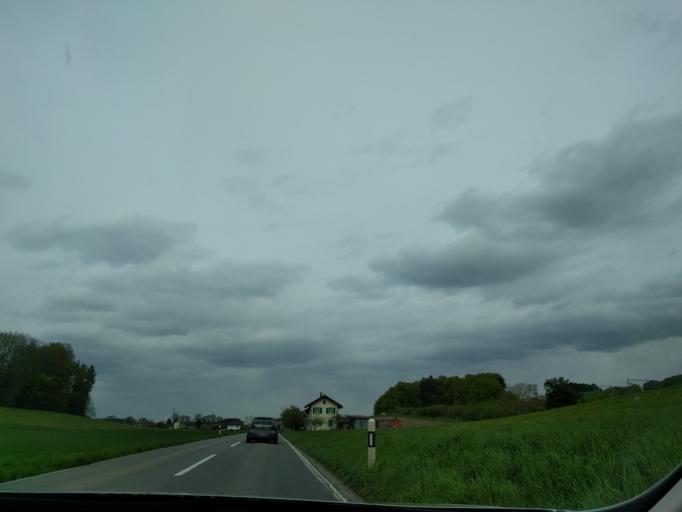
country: CH
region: Fribourg
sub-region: Sense District
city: Dudingen
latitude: 46.8628
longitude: 7.2028
